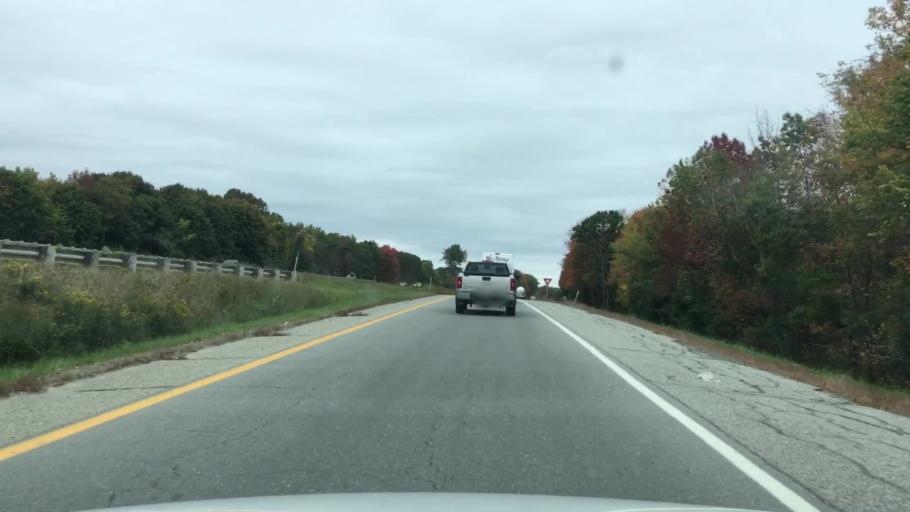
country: US
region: Maine
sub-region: Kennebec County
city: Oakland
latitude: 44.5472
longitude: -69.6786
